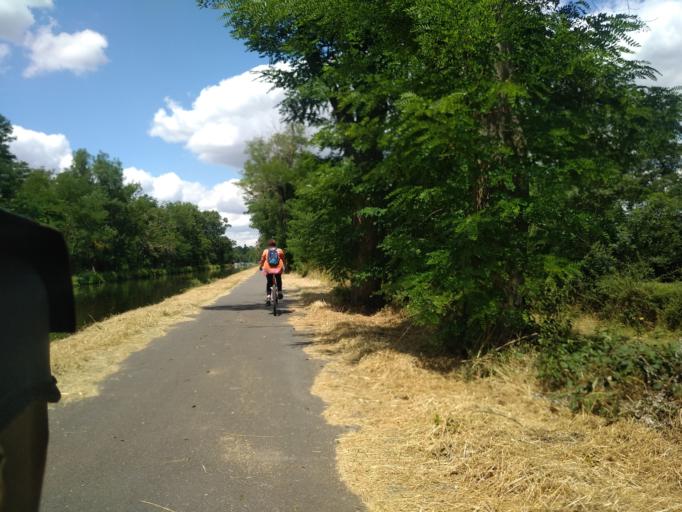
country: FR
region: Rhone-Alpes
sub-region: Departement de la Loire
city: Briennon
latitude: 46.1353
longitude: 4.0822
